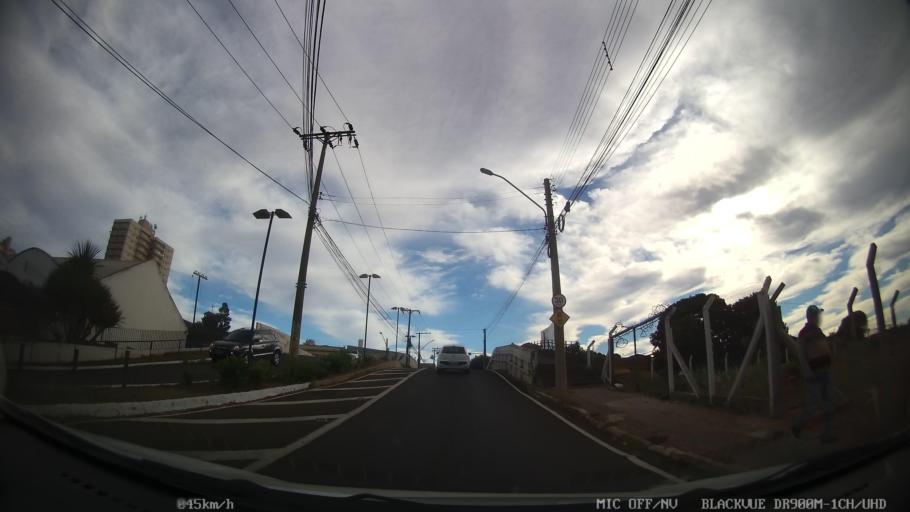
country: BR
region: Sao Paulo
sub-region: Catanduva
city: Catanduva
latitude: -21.1307
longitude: -48.9686
